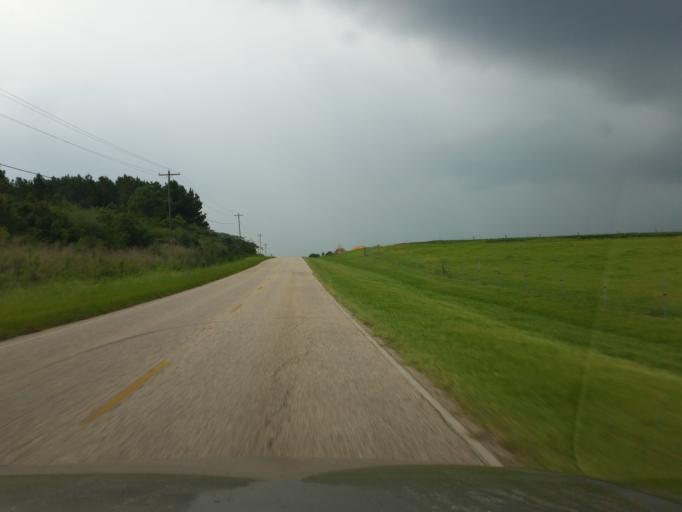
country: US
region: Alabama
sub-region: Baldwin County
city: Robertsdale
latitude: 30.5626
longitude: -87.5816
